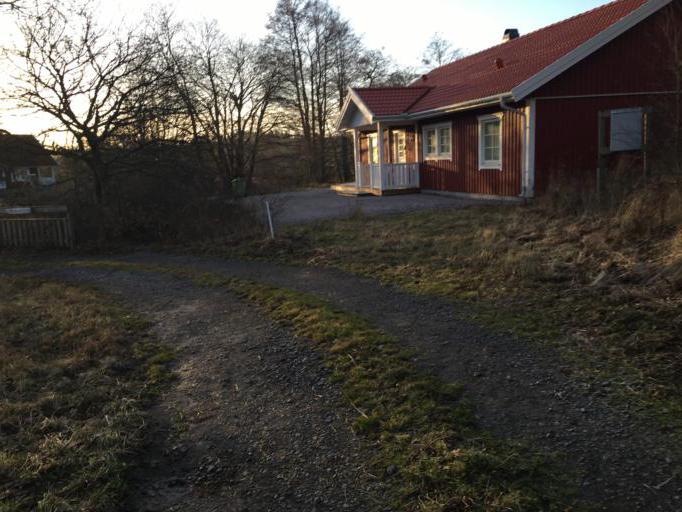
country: SE
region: Kalmar
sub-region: Vasterviks Kommun
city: Vaestervik
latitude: 57.6270
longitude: 16.5289
